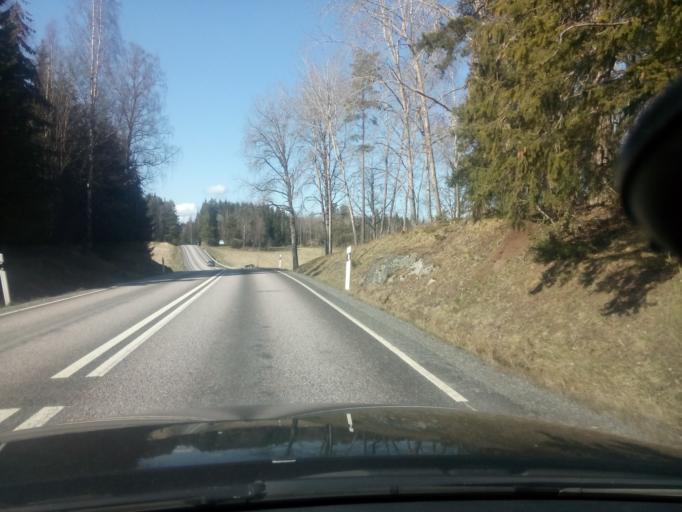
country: SE
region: Soedermanland
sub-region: Nykopings Kommun
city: Stigtomta
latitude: 58.9656
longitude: 16.8543
